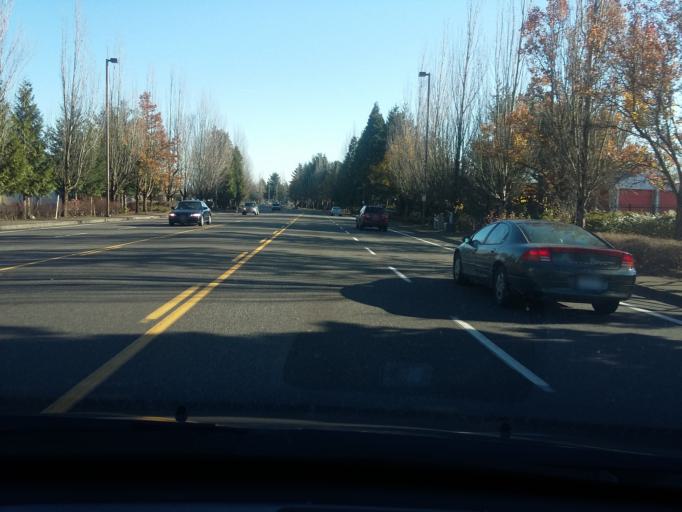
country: US
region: Washington
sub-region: Clark County
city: Mill Plain
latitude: 45.5623
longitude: -122.5253
